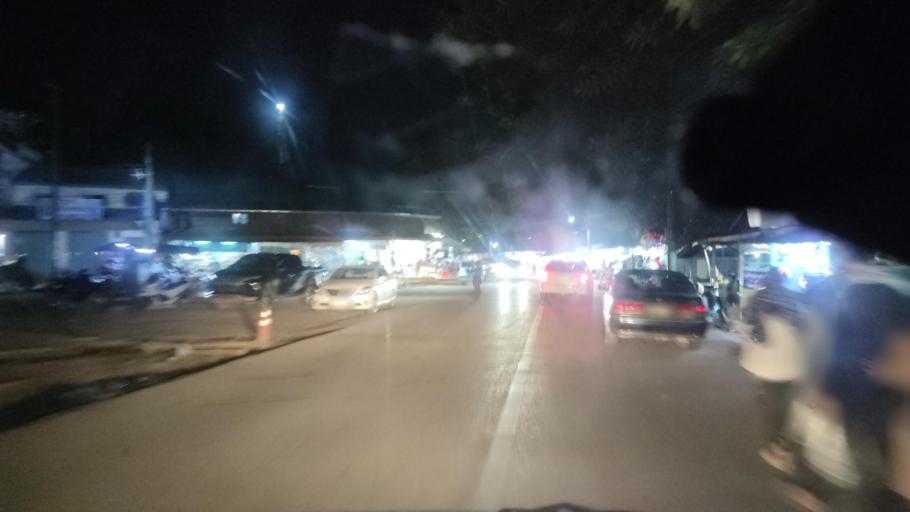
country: TH
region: Chiang Rai
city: Mae Sai
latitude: 21.2902
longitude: 99.6025
